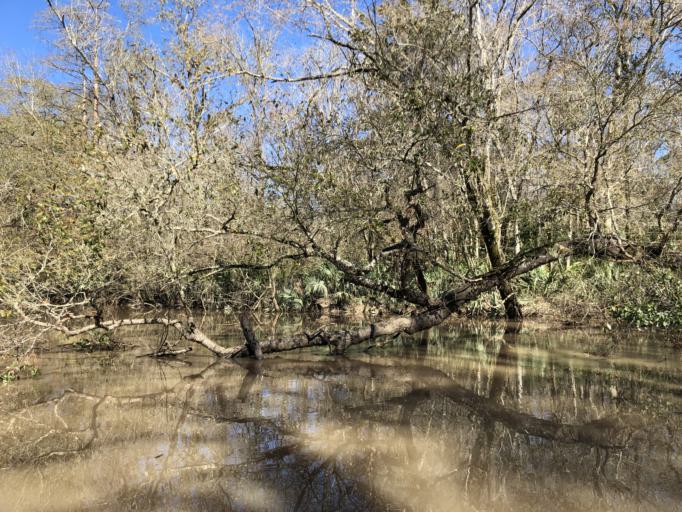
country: US
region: Louisiana
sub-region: Calcasieu Parish
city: Iowa
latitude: 30.3084
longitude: -93.0702
